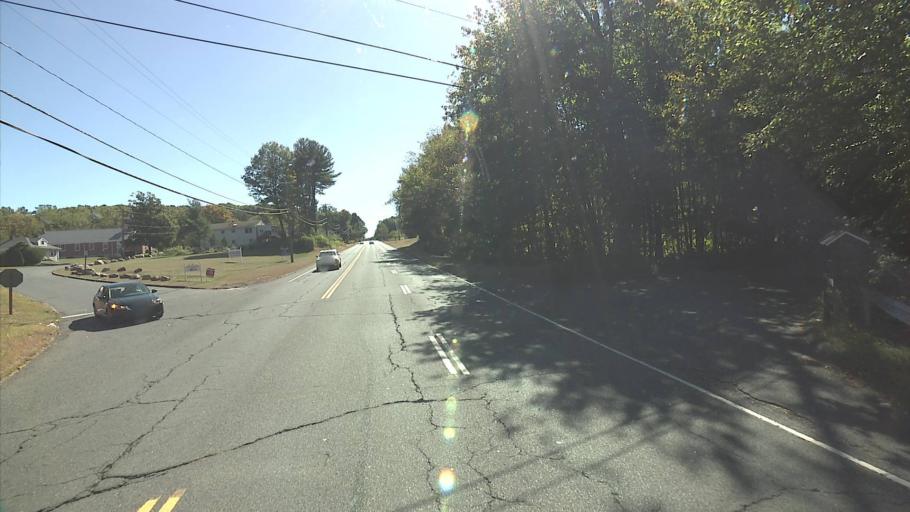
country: US
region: Connecticut
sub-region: New Haven County
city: Prospect
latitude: 41.5310
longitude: -73.0084
